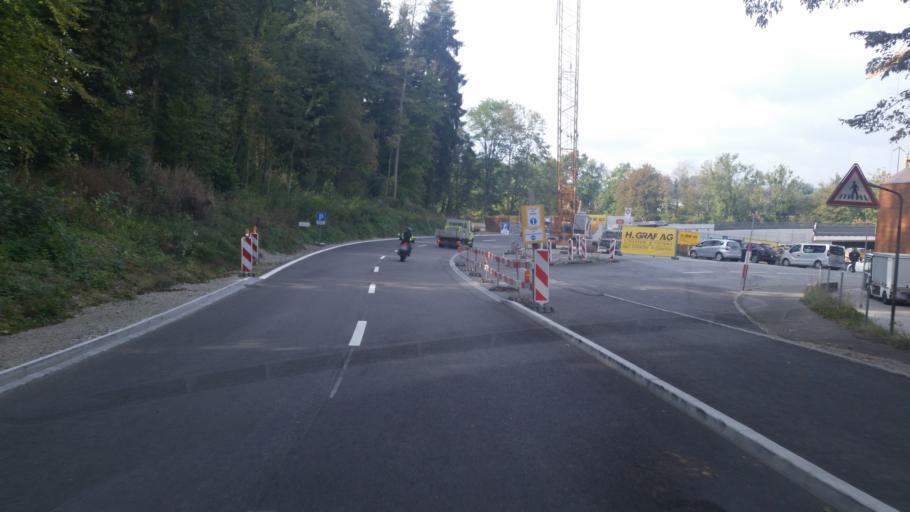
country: CH
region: Aargau
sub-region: Bezirk Baden
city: Kunten
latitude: 47.3927
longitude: 8.3022
